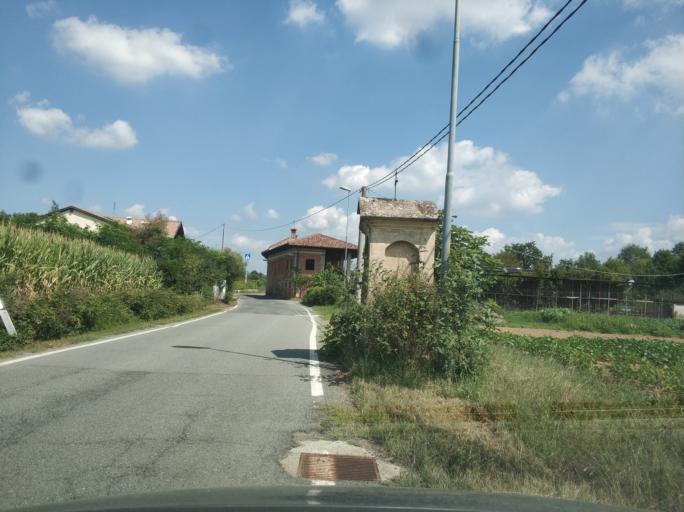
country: IT
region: Piedmont
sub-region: Provincia di Torino
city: Rivarossa
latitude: 45.2453
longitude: 7.7062
